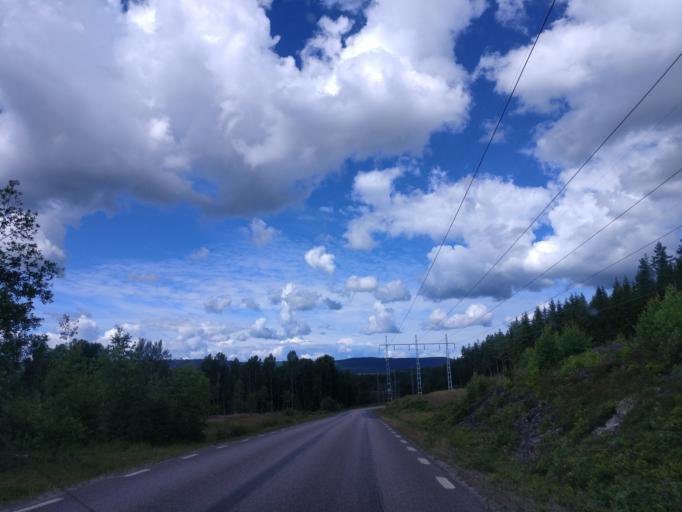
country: SE
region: Vaermland
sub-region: Hagfors Kommun
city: Hagfors
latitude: 60.0409
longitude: 13.5359
